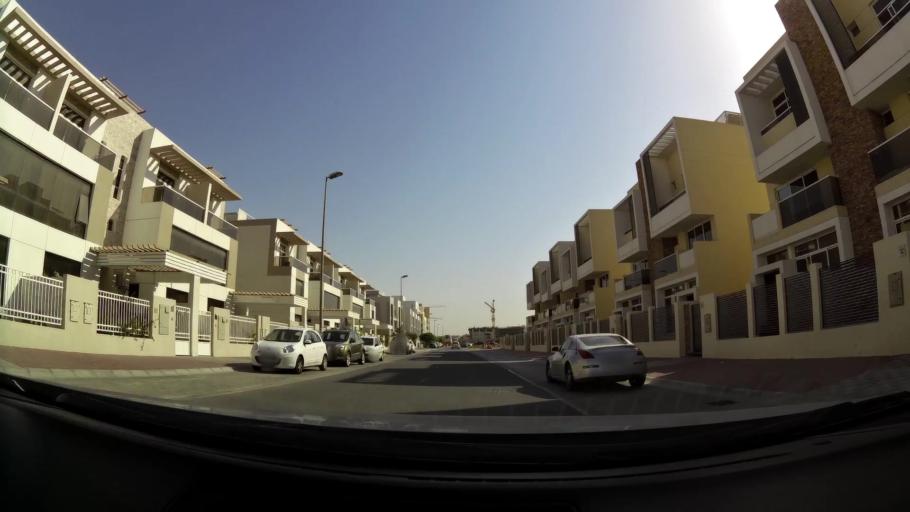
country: AE
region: Dubai
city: Dubai
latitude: 25.0648
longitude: 55.2034
